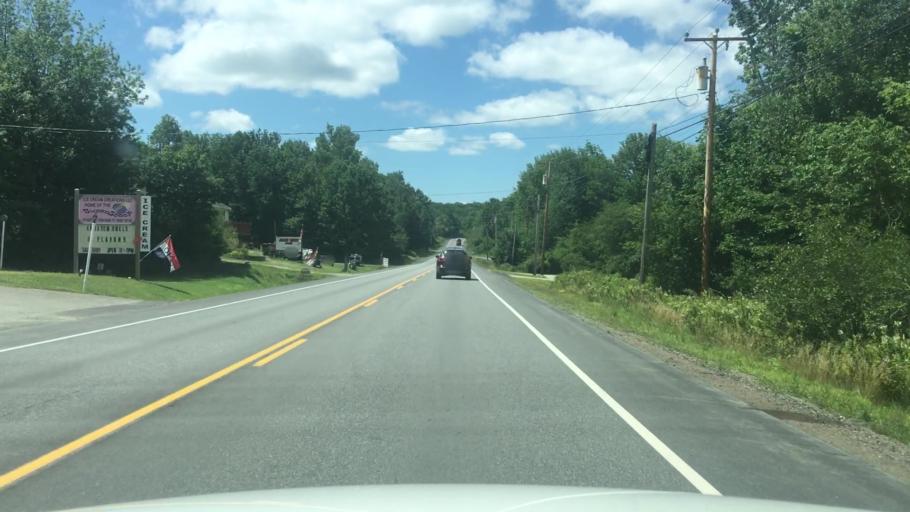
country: US
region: Maine
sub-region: Waldo County
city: Searsmont
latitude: 44.4019
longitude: -69.1137
